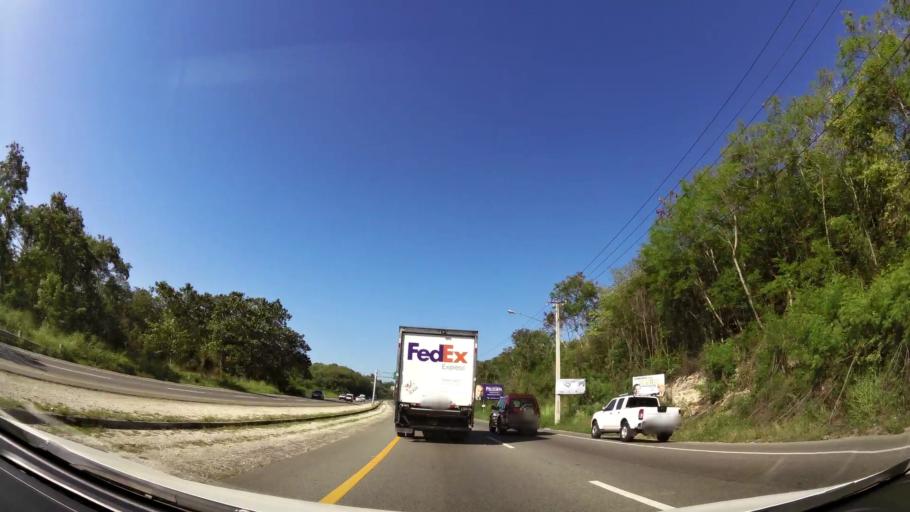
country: DO
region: San Cristobal
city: El Carril
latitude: 18.4371
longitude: -70.0246
